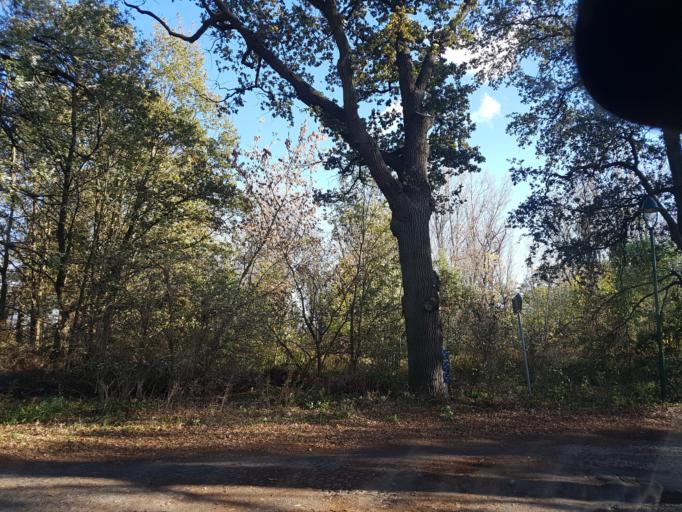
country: DE
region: Brandenburg
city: Nauen
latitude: 52.6366
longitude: 12.9080
